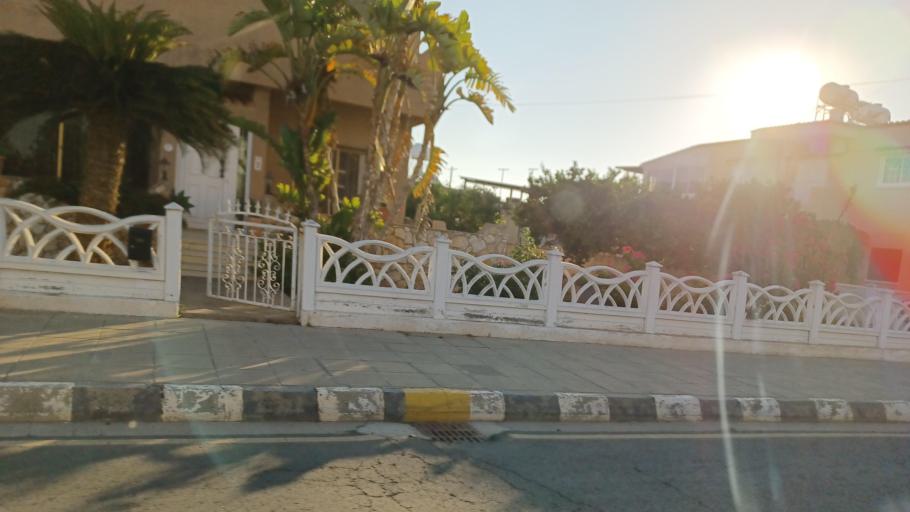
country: CY
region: Larnaka
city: Xylotymbou
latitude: 35.0325
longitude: 33.7650
